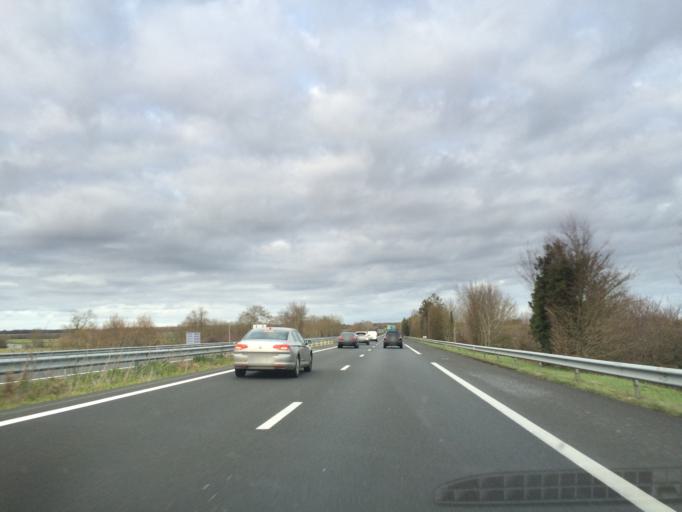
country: FR
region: Poitou-Charentes
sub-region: Departement de la Charente-Maritime
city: Saint-Jean-d'Angely
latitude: 46.0632
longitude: -0.5348
